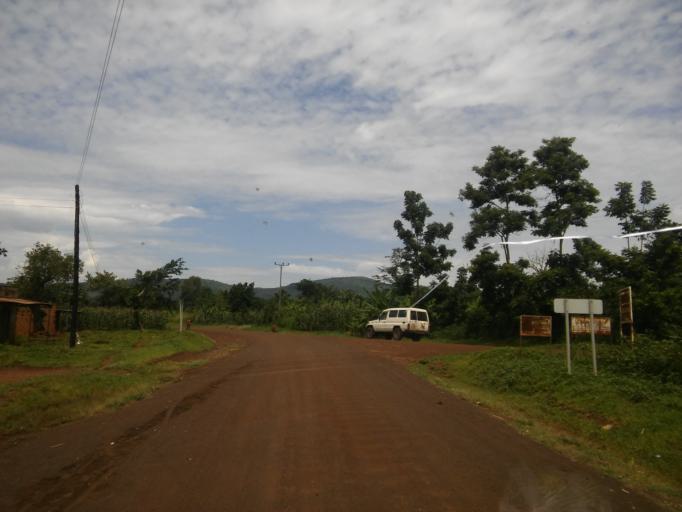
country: UG
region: Eastern Region
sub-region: Manafwa District
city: Manafwa
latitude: 0.8343
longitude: 34.2839
